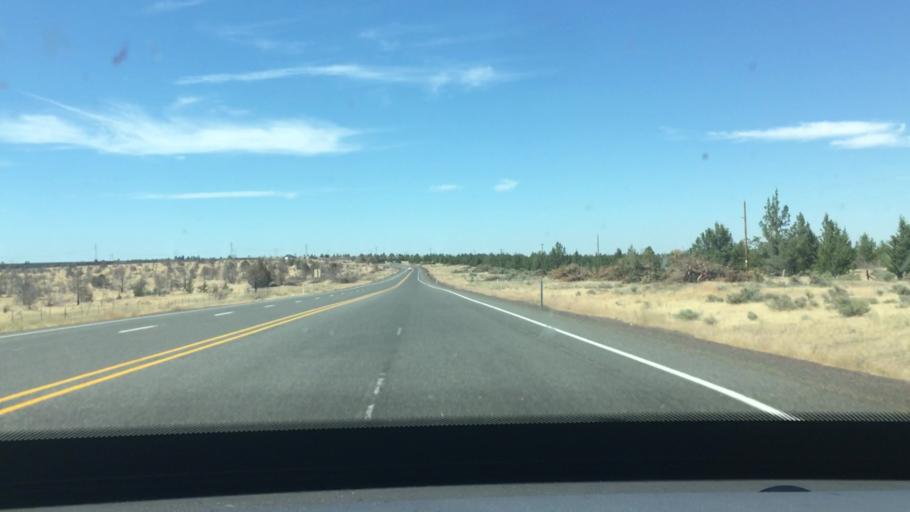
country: US
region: Oregon
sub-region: Jefferson County
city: Madras
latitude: 44.9059
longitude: -120.9388
